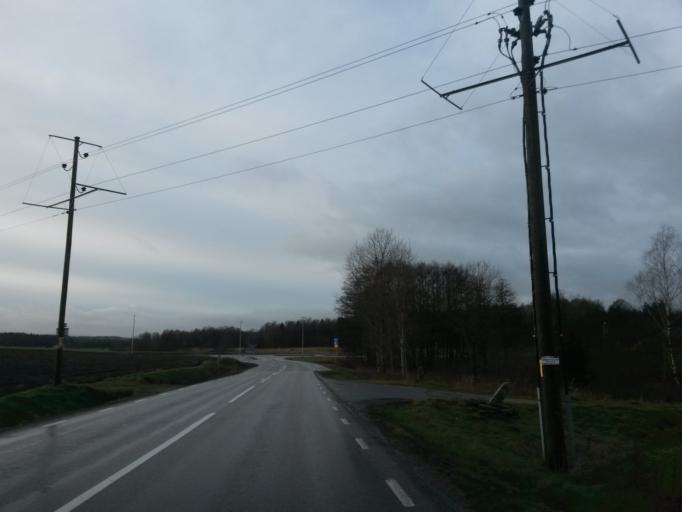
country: SE
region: Vaestra Goetaland
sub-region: Harryda Kommun
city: Ravlanda
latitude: 57.5550
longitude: 12.5251
